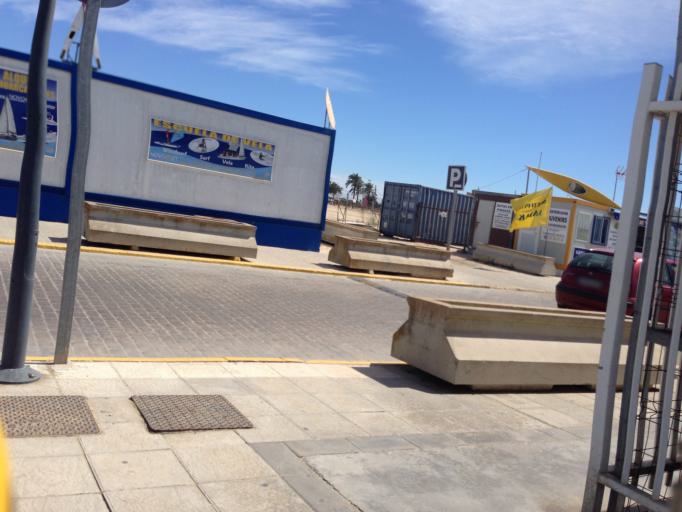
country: ES
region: Andalusia
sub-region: Provincia de Cadiz
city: Chiclana de la Frontera
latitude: 36.3946
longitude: -6.2088
